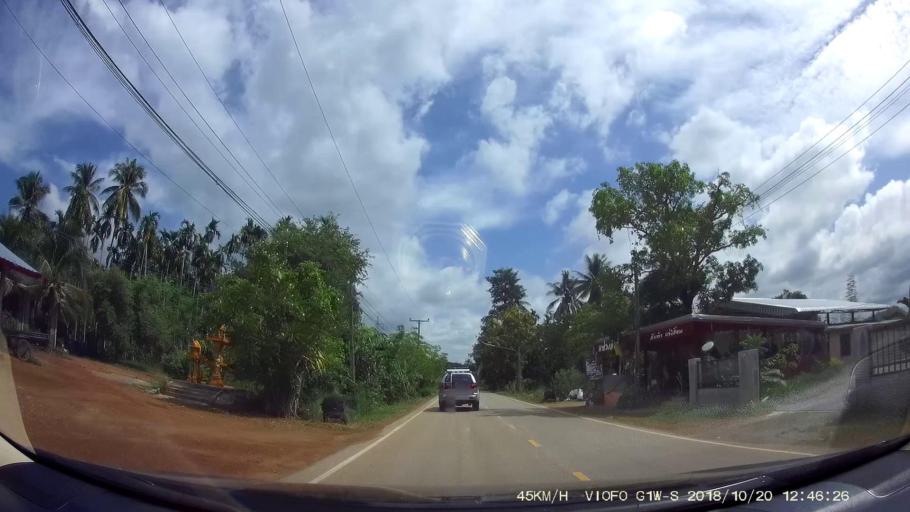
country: TH
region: Chaiyaphum
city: Khon San
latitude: 16.5336
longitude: 101.8802
